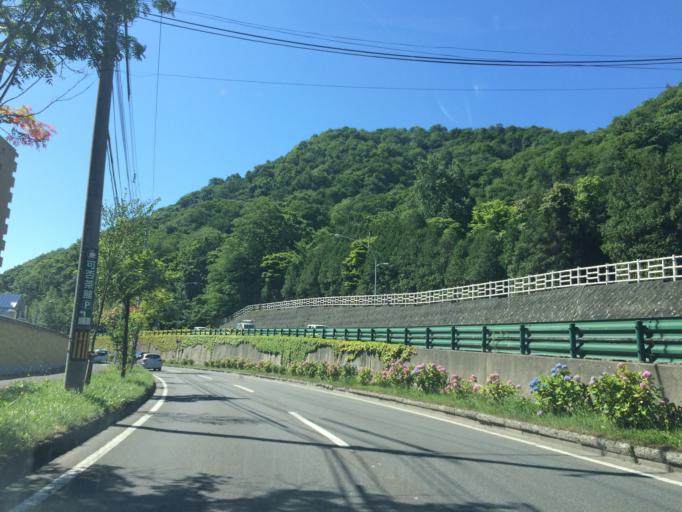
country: JP
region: Hokkaido
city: Sapporo
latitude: 43.0521
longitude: 141.3165
